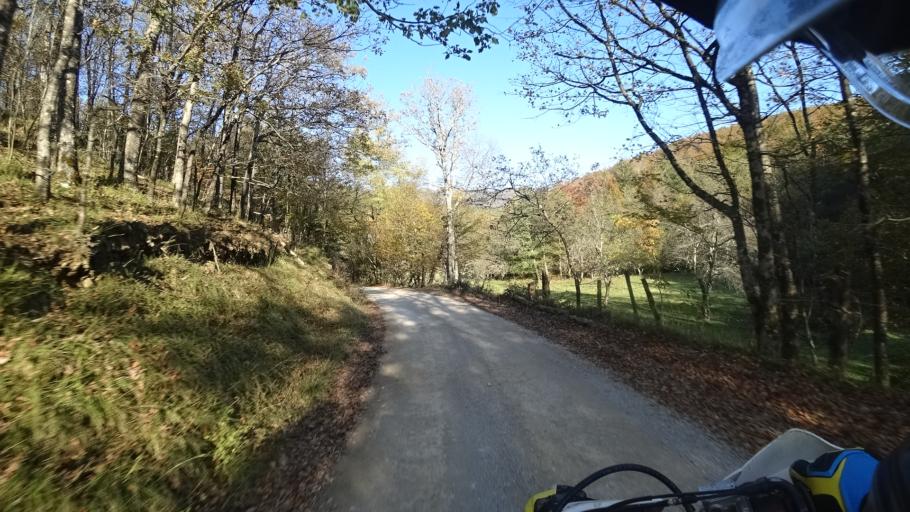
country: HR
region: Primorsko-Goranska
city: Klana
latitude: 45.5057
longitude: 14.3506
